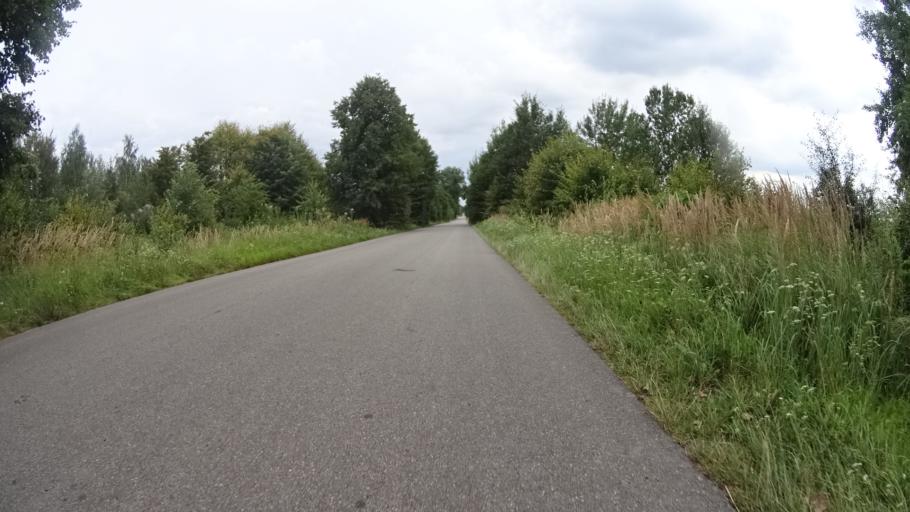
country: PL
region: Masovian Voivodeship
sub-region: Powiat grojecki
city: Goszczyn
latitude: 51.6782
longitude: 20.8595
